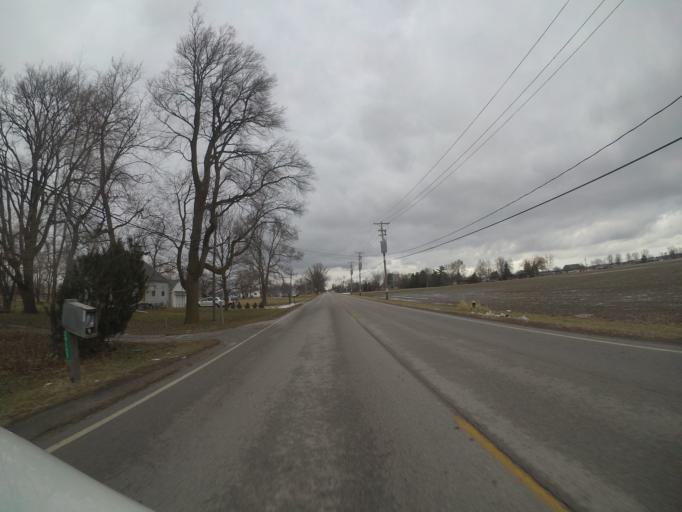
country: US
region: Ohio
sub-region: Wood County
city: Walbridge
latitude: 41.5754
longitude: -83.5122
